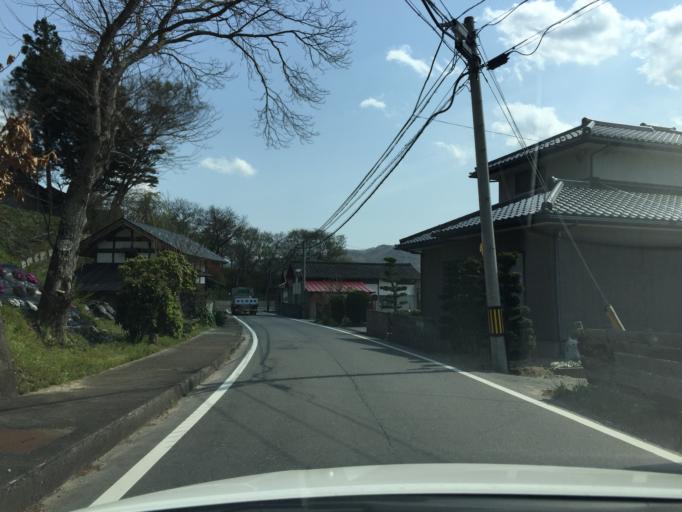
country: JP
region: Fukushima
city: Namie
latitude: 37.3478
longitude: 140.8036
